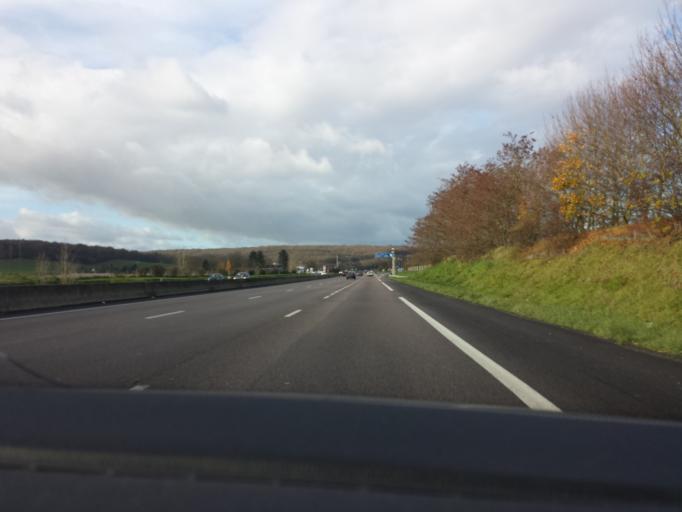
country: FR
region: Ile-de-France
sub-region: Departement des Yvelines
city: Rosny-sur-Seine
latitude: 48.9915
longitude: 1.6405
